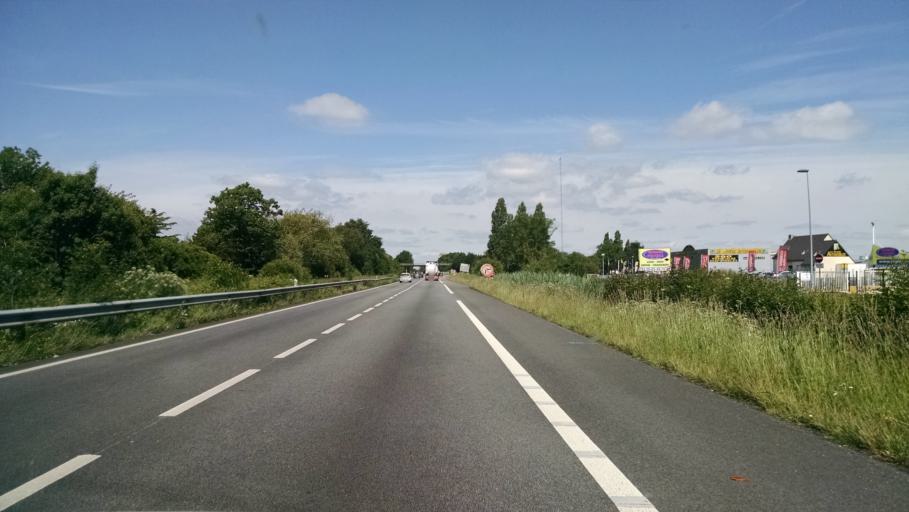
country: FR
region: Pays de la Loire
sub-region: Departement de la Loire-Atlantique
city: Vigneux-de-Bretagne
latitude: 47.2980
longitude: -1.7506
